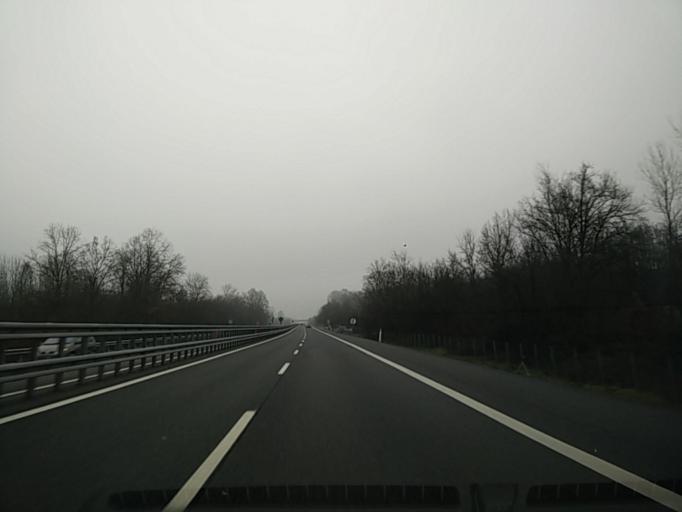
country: IT
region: Piedmont
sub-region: Provincia di Asti
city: Dusino
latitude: 44.9360
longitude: 7.9920
